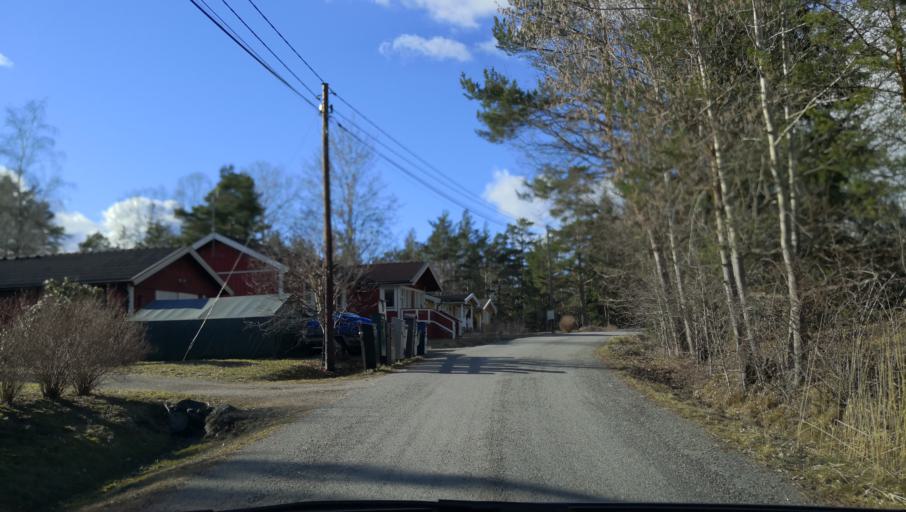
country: SE
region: Stockholm
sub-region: Varmdo Kommun
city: Hemmesta
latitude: 59.2418
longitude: 18.5188
